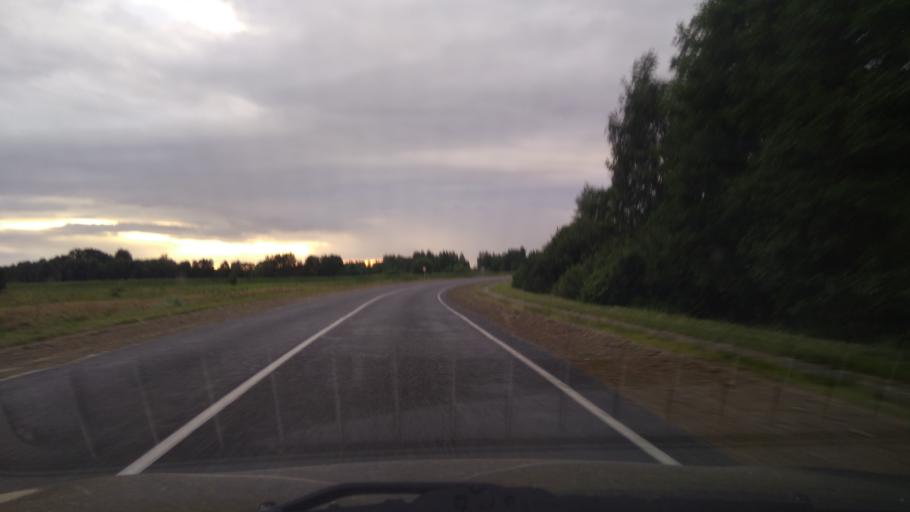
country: BY
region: Brest
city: Byaroza
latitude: 52.4161
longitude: 24.9822
